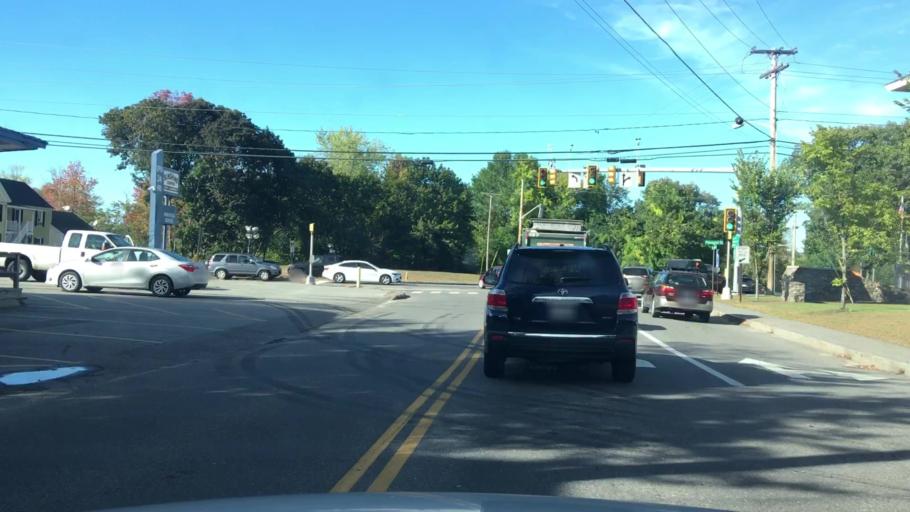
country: US
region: Maine
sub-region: Cumberland County
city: Brunswick
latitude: 43.9125
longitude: -69.9762
